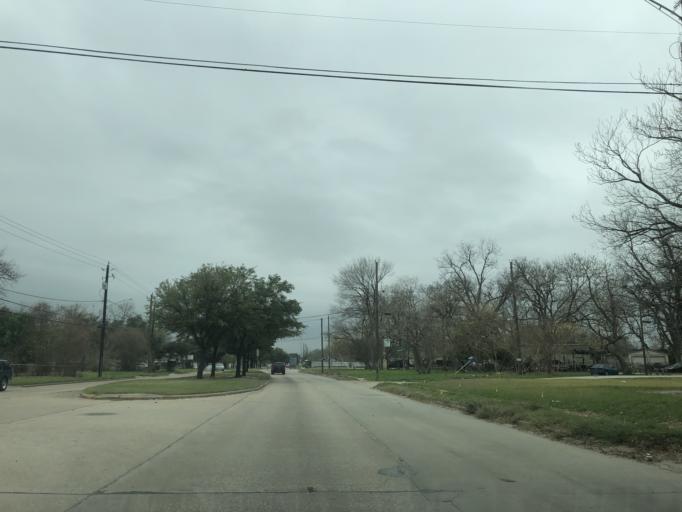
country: US
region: Texas
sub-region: Harris County
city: Jacinto City
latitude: 29.8245
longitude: -95.2845
